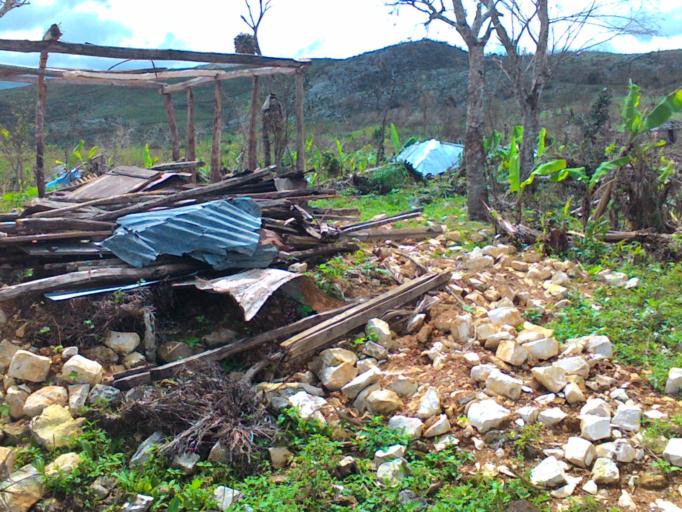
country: HT
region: Grandans
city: Jeremie
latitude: 18.4879
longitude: -74.1081
